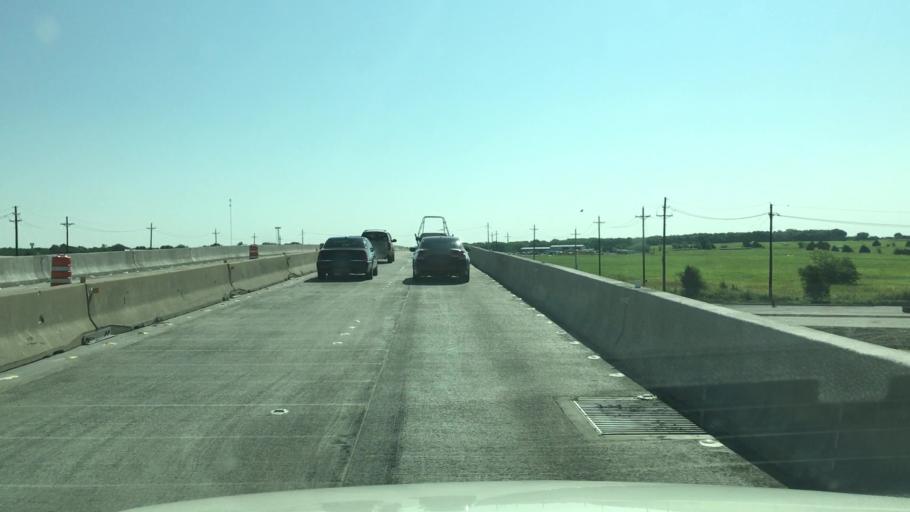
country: US
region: Texas
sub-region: Rockwall County
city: Rockwall
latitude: 32.9192
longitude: -96.4193
